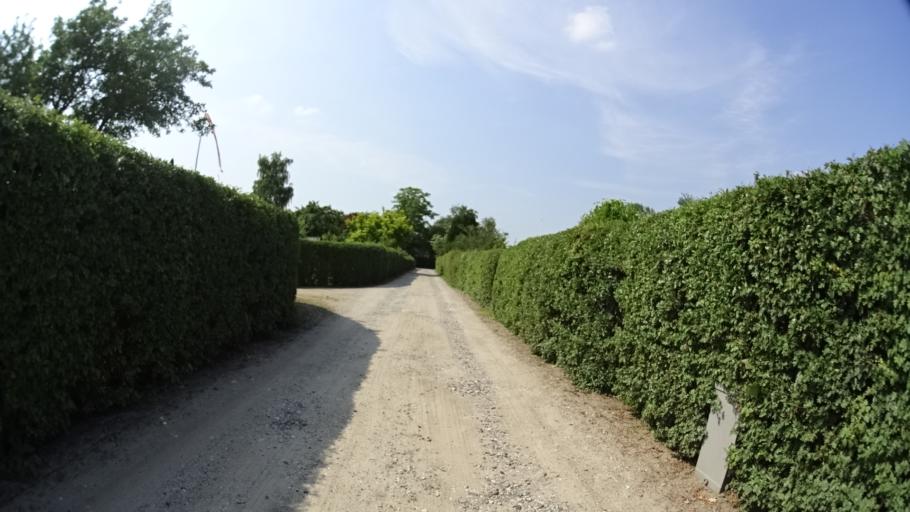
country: DK
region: Central Jutland
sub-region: Arhus Kommune
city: Arhus
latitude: 56.1474
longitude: 10.1652
